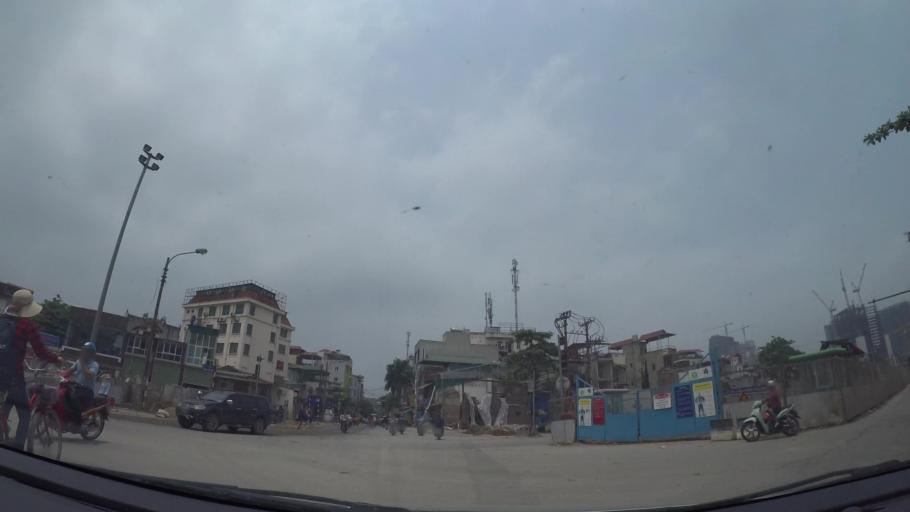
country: VN
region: Ha Noi
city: Tay Ho
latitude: 21.0774
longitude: 105.7875
